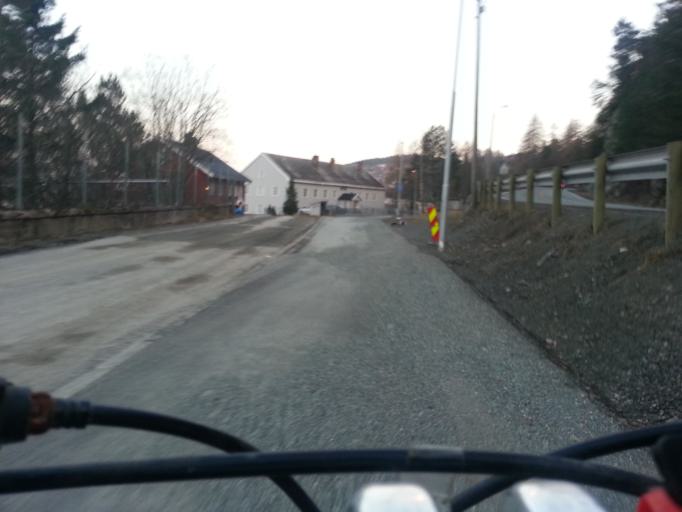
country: NO
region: Sor-Trondelag
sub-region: Trondheim
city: Trondheim
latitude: 63.4382
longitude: 10.3488
